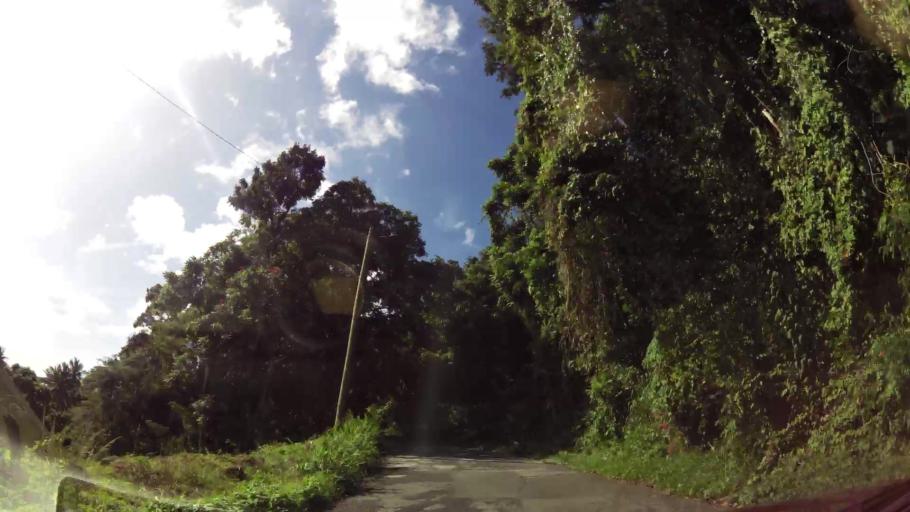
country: DM
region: Saint Luke
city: Pointe Michel
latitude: 15.2794
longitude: -61.3717
